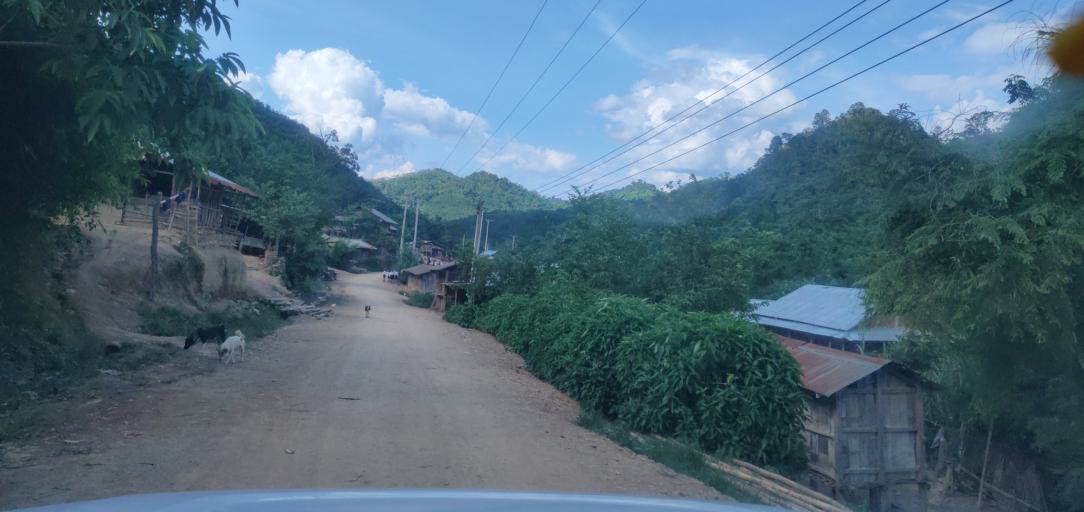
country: LA
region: Phongsali
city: Phongsali
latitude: 21.4633
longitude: 102.0781
